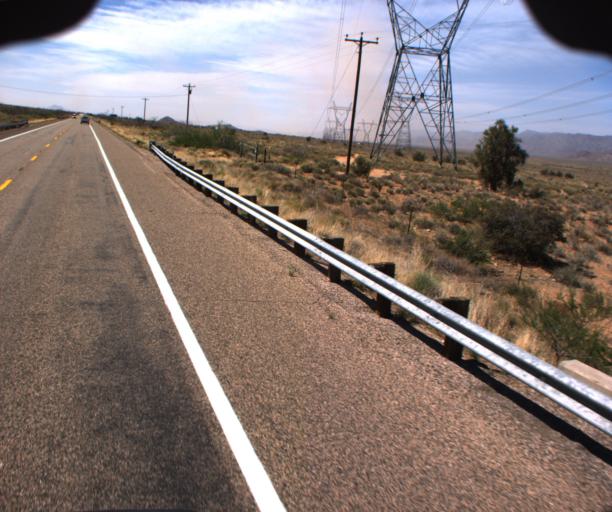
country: US
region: Arizona
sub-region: Mohave County
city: New Kingman-Butler
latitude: 35.3972
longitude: -113.7538
